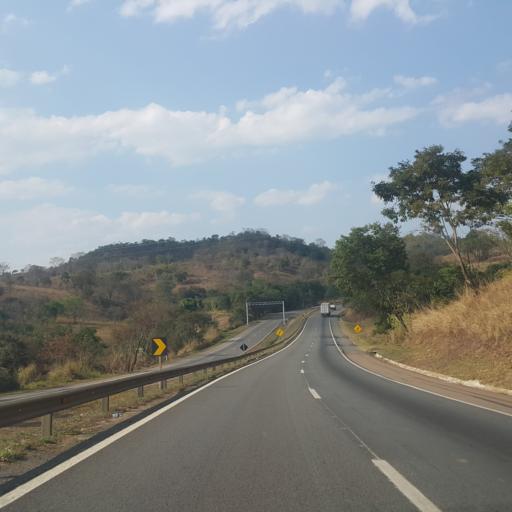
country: BR
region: Goias
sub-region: Abadiania
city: Abadiania
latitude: -16.1126
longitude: -48.5873
